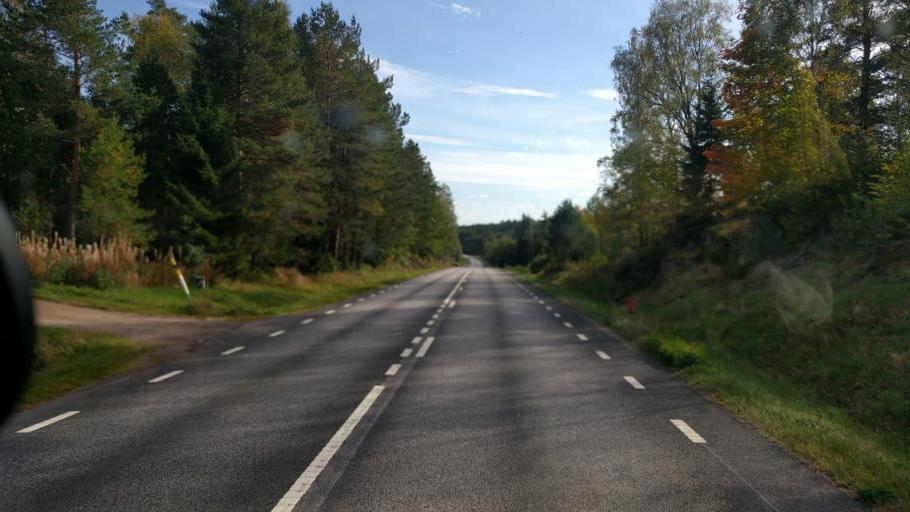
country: SE
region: OEstergoetland
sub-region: Kinda Kommun
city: Kisa
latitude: 57.9184
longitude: 15.6815
